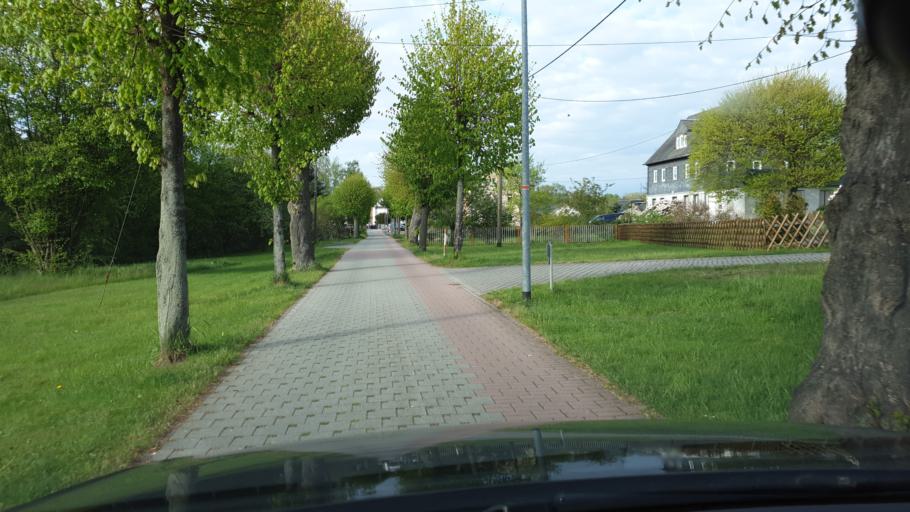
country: DE
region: Saxony
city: Mittweida
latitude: 50.9710
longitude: 12.9699
